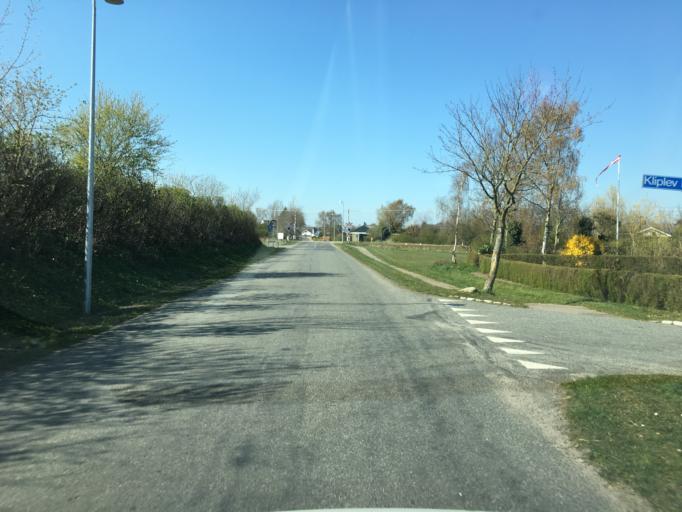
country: DK
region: South Denmark
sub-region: Aabenraa Kommune
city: Krusa
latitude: 54.9338
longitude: 9.4081
